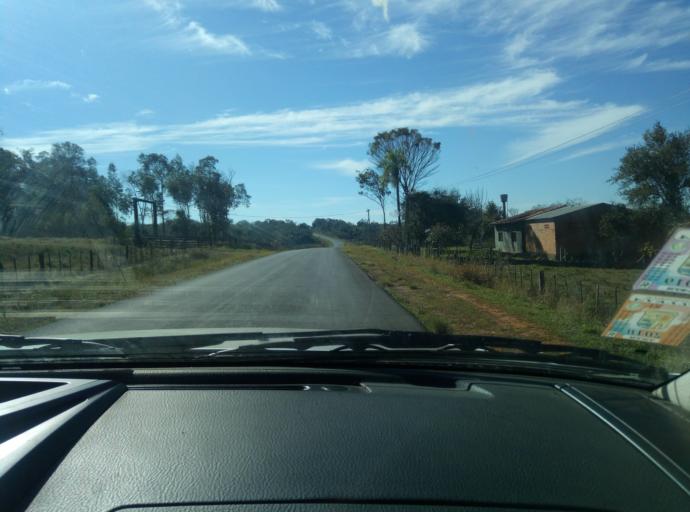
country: PY
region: Caaguazu
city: Carayao
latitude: -25.1742
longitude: -56.3135
